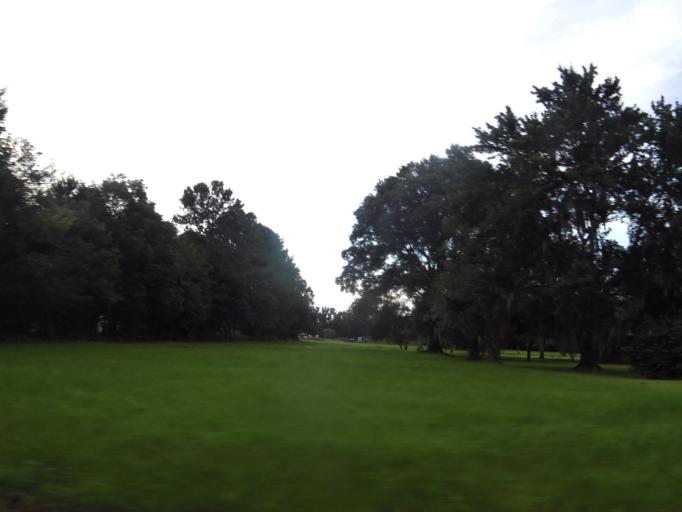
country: US
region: Florida
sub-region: Duval County
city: Jacksonville
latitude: 30.3453
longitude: -81.7889
